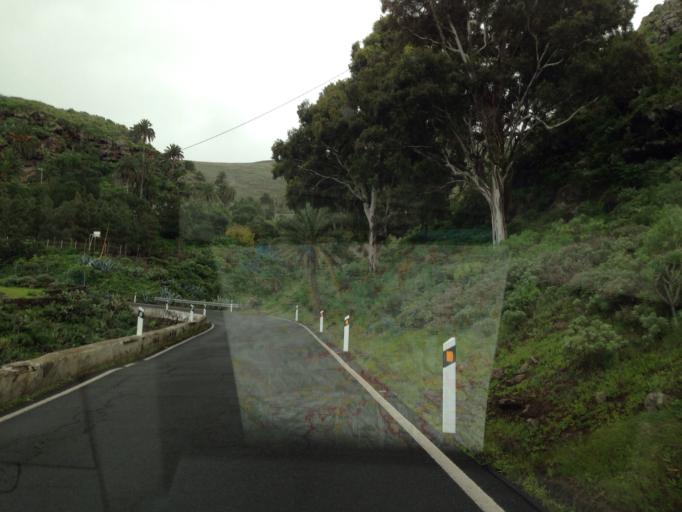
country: ES
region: Canary Islands
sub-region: Provincia de Las Palmas
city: Guia
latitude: 28.1158
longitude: -15.6495
